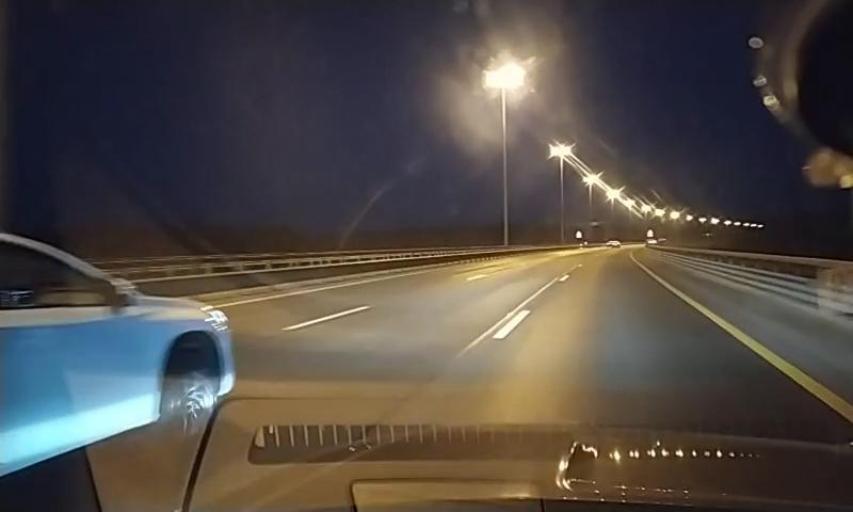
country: RU
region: St.-Petersburg
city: Pesochnyy
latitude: 60.0848
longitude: 30.1055
